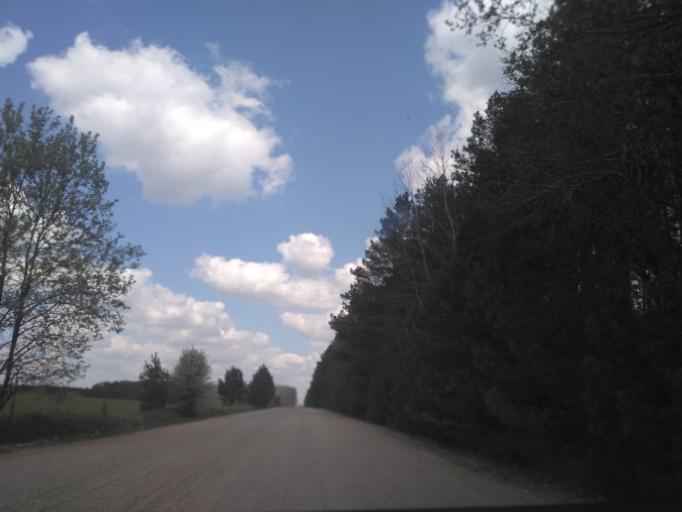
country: BY
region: Minsk
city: Radashkovichy
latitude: 54.2328
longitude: 27.2894
